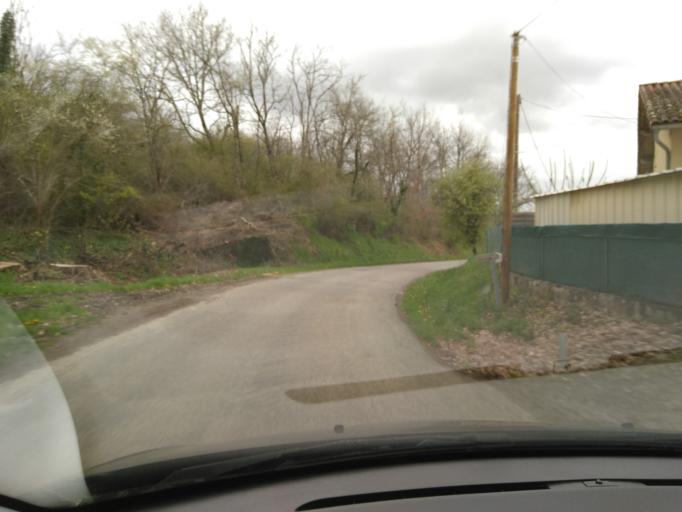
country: FR
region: Midi-Pyrenees
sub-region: Departement du Tarn-et-Garonne
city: Saint-Porquier
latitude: 43.9601
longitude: 1.1304
